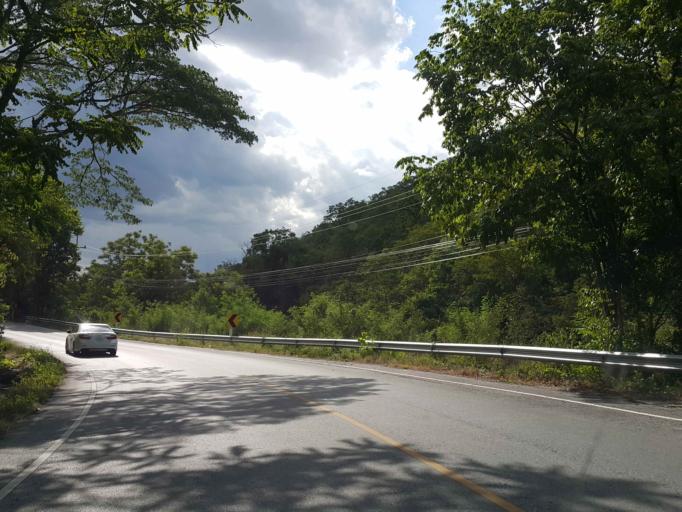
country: TH
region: Lampang
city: Thoen
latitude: 17.6455
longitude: 99.3021
